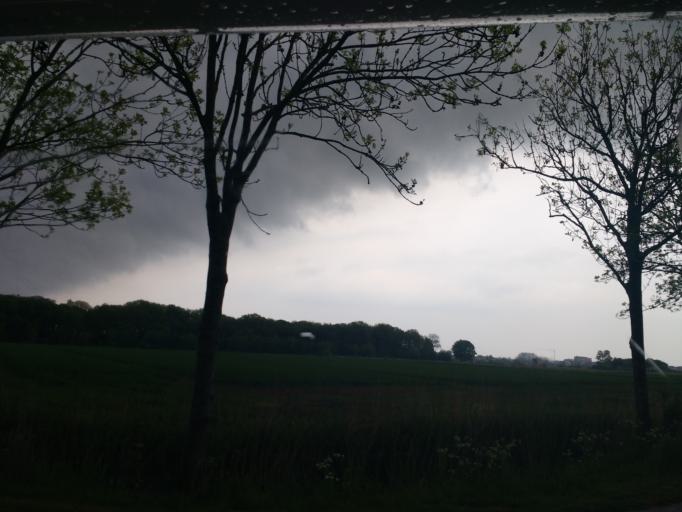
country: DE
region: Lower Saxony
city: Schillig
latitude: 53.7038
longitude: 8.0037
